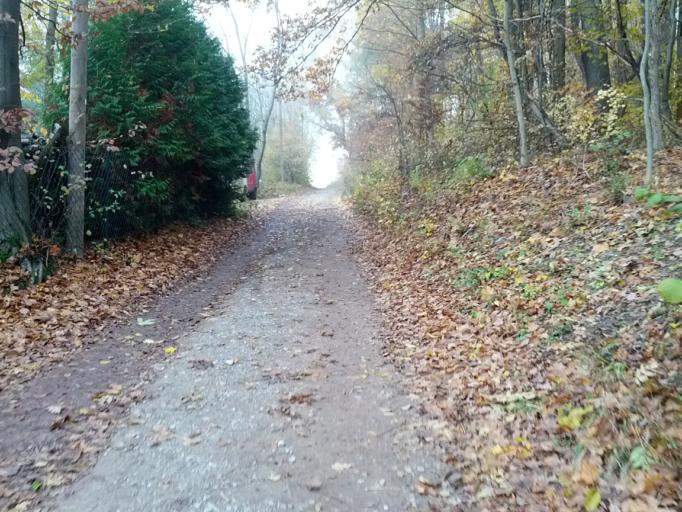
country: DE
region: Thuringia
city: Eisenach
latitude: 50.9886
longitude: 10.3391
